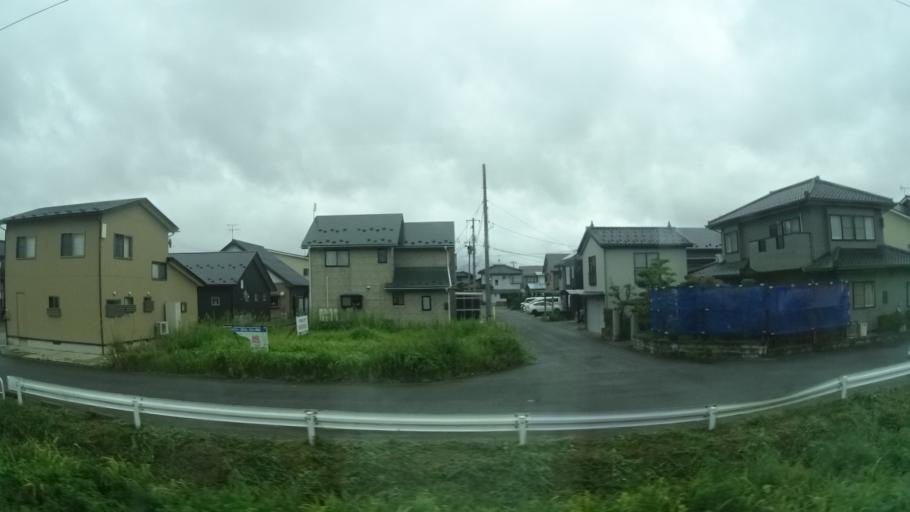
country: JP
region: Yamagata
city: Tsuruoka
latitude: 38.7413
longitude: 139.8106
